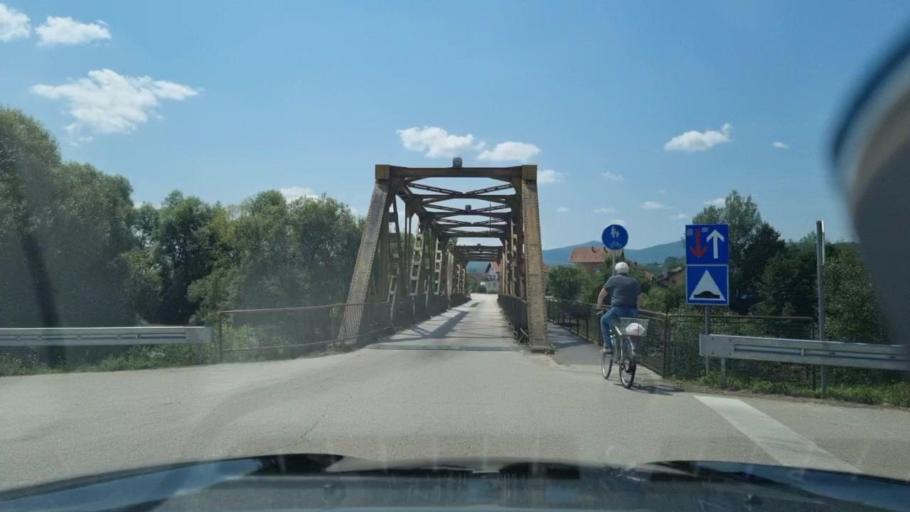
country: BA
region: Federation of Bosnia and Herzegovina
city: Sanski Most
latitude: 44.7571
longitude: 16.6752
